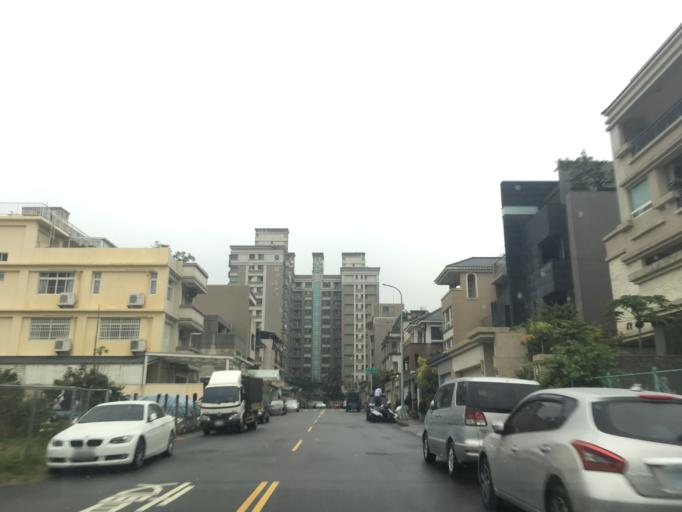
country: TW
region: Taiwan
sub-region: Taichung City
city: Taichung
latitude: 24.1696
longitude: 120.7160
